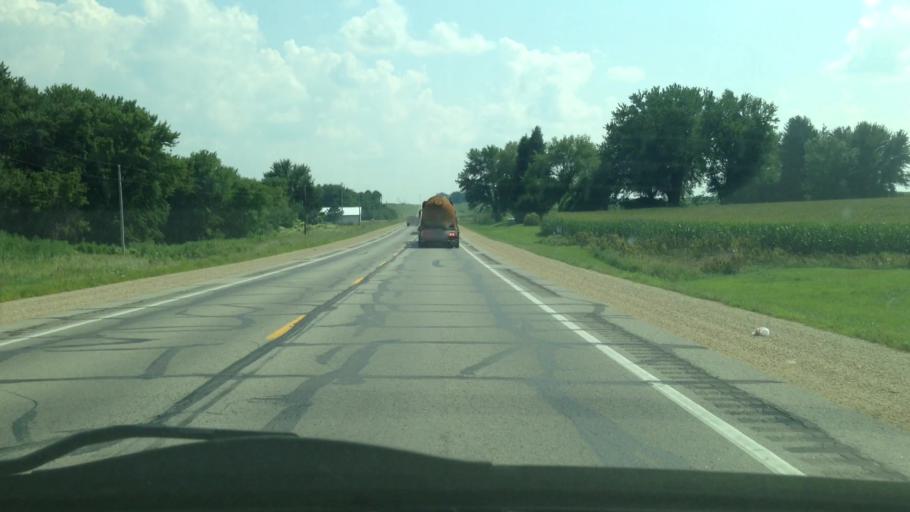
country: US
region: Iowa
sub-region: Chickasaw County
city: New Hampton
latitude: 43.1727
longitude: -92.2987
